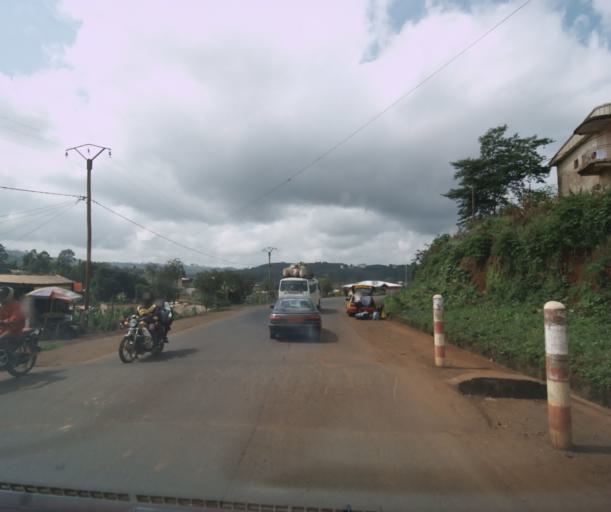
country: CM
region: West
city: Dschang
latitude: 5.4556
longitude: 10.0687
